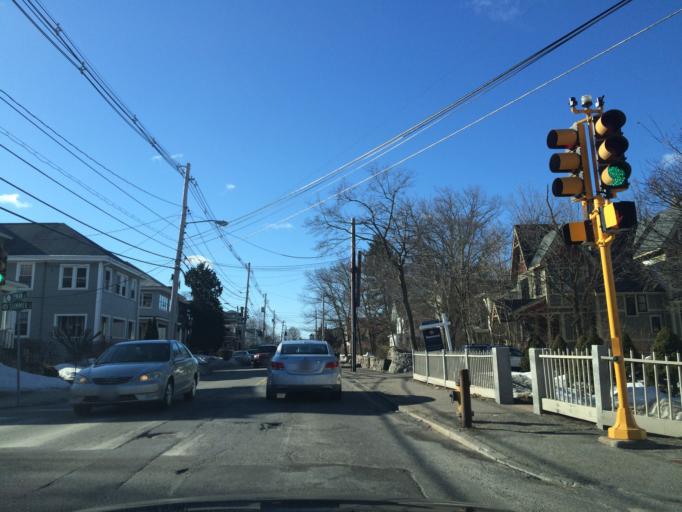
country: US
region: Massachusetts
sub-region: Middlesex County
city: Waltham
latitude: 42.3798
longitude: -71.2306
